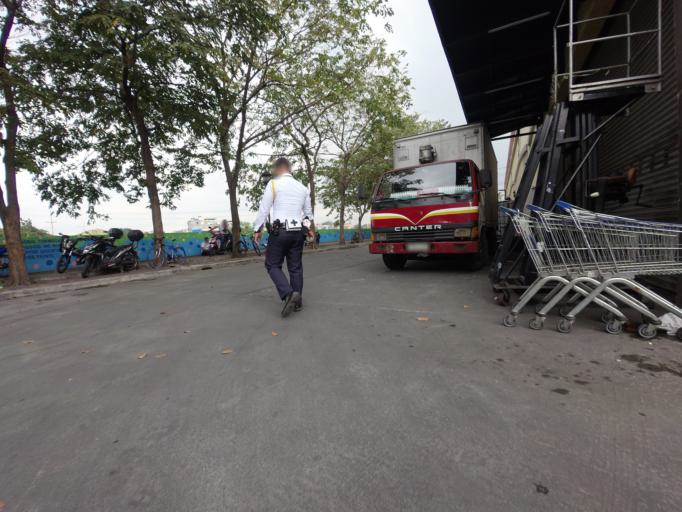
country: PH
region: Metro Manila
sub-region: San Juan
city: San Juan
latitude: 14.5817
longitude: 121.0112
